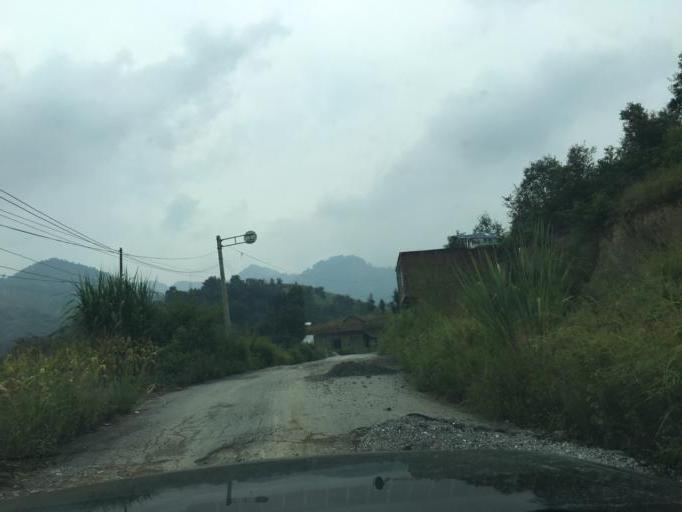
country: CN
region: Guangxi Zhuangzu Zizhiqu
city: Tongle
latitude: 25.1124
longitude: 106.2705
